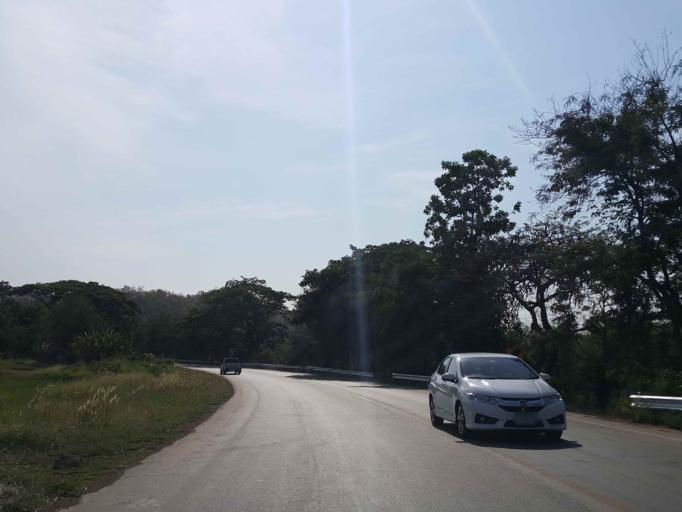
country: TH
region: Sukhothai
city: Thung Saliam
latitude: 17.3439
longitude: 99.5975
